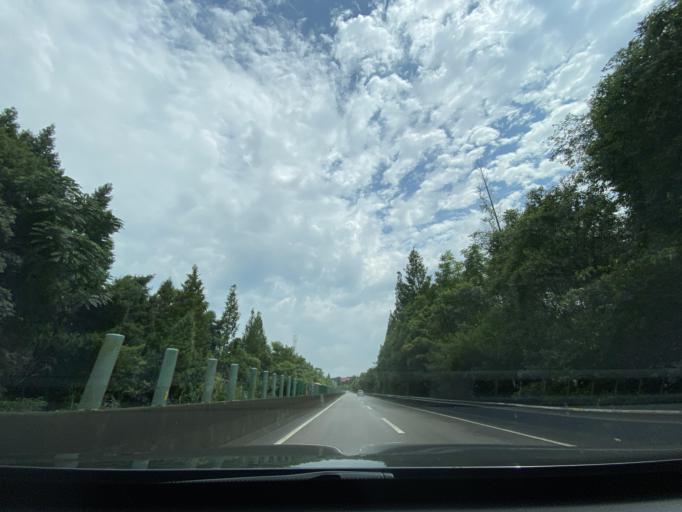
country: CN
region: Sichuan
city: Jiancheng
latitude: 30.2678
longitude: 104.6047
